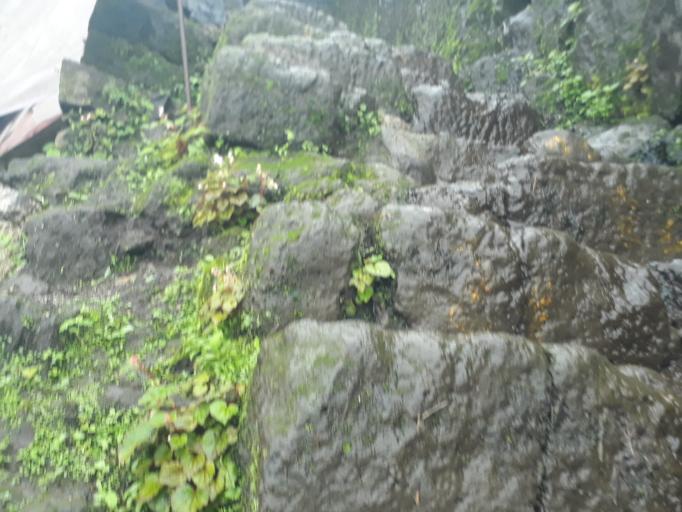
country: IN
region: Maharashtra
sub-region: Pune Division
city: Lonavla
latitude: 18.6321
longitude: 73.5127
